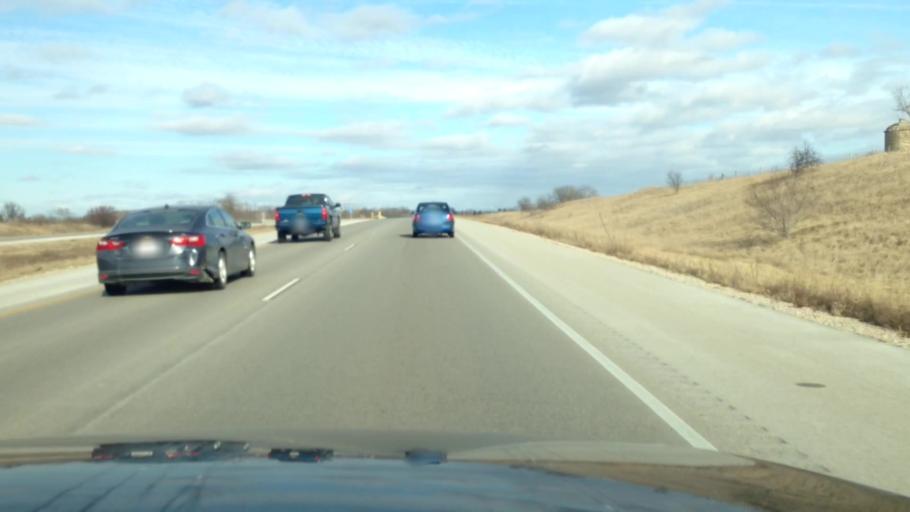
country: US
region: Wisconsin
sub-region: Waukesha County
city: Big Bend
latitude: 42.8968
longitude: -88.2629
